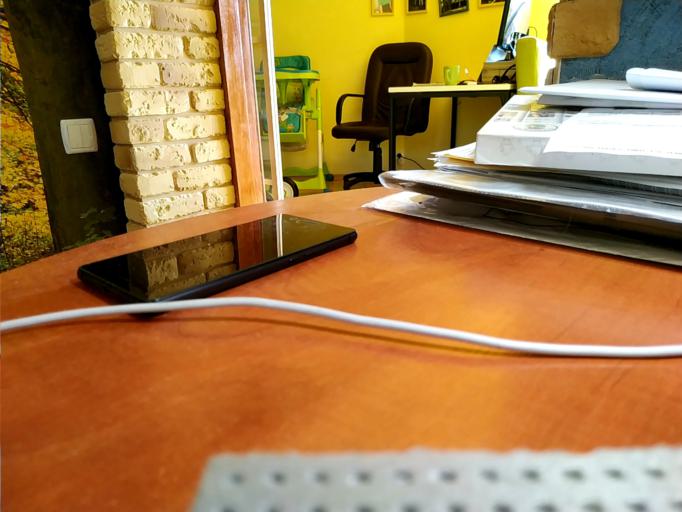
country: RU
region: Tverskaya
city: Kalashnikovo
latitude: 57.3703
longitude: 35.4155
